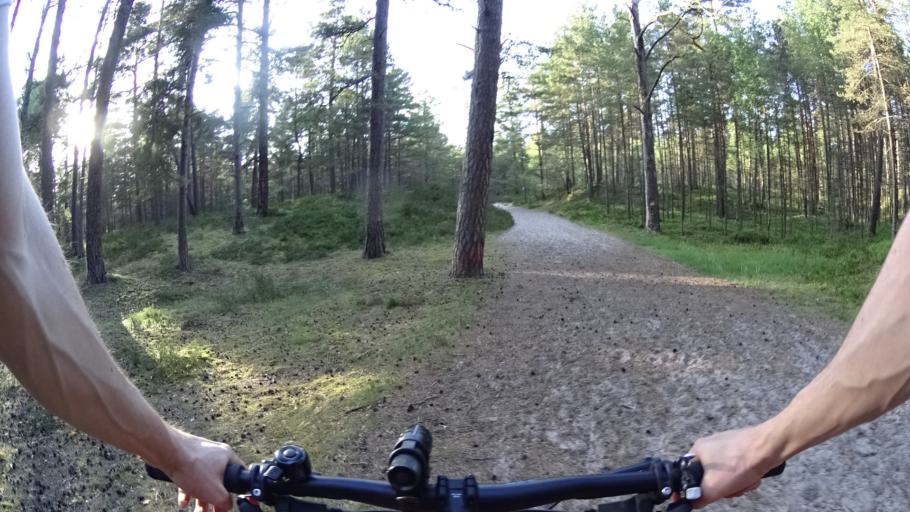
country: LV
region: Riga
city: Jaunciems
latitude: 57.0943
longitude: 24.1572
